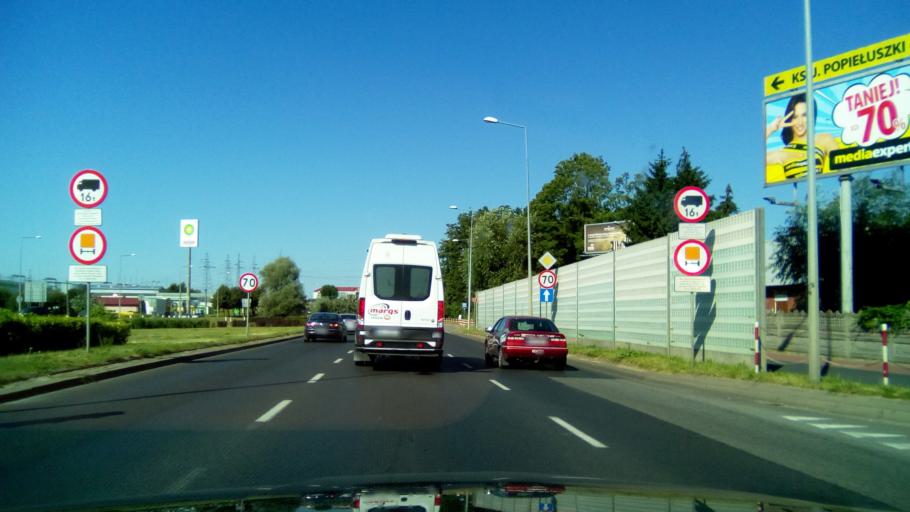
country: PL
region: Masovian Voivodeship
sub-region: Plock
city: Plock
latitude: 52.5389
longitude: 19.7427
